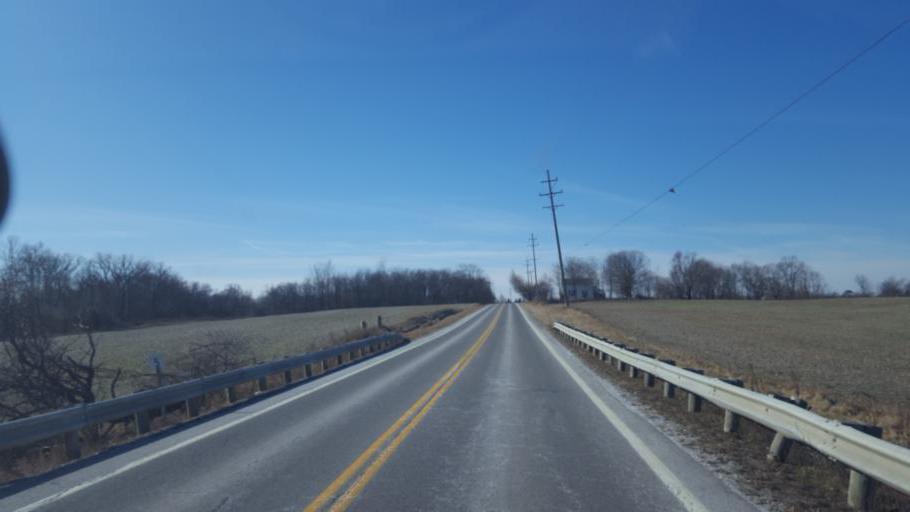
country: US
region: Ohio
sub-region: Marion County
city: Marion
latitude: 40.5456
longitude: -83.1970
